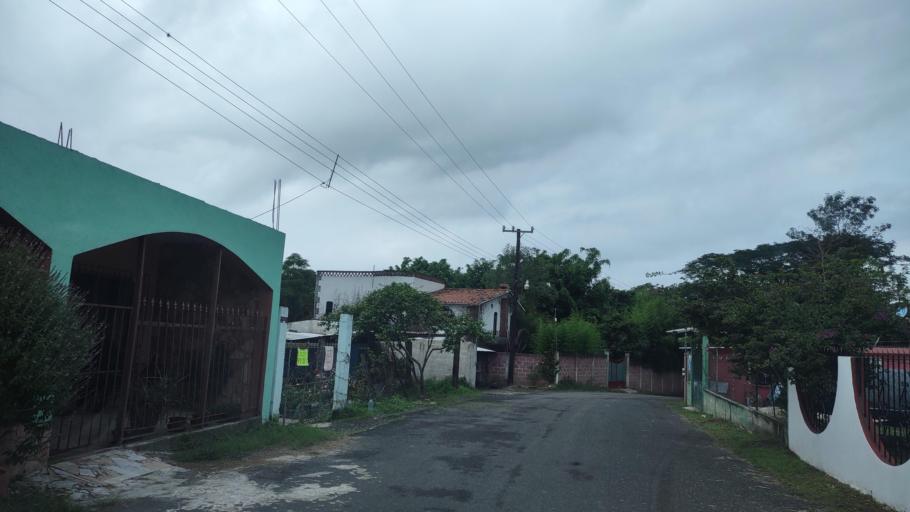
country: MX
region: Veracruz
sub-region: Coatepec
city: Bella Esperanza
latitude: 19.4487
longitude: -96.8284
